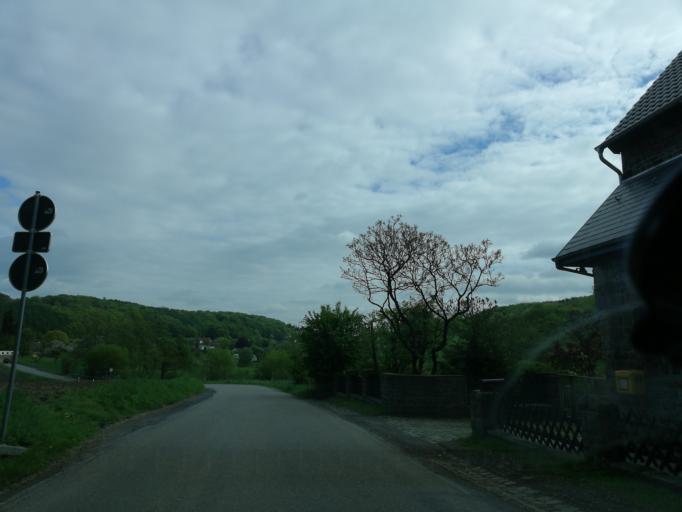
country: DE
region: North Rhine-Westphalia
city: Gevelsberg
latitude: 51.3676
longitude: 7.3103
